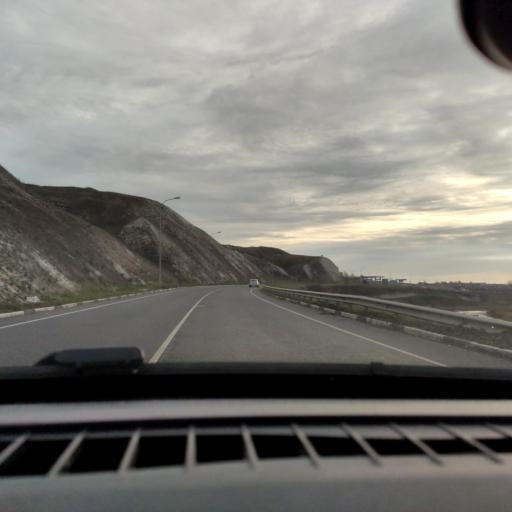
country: RU
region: Belgorod
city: Alekseyevka
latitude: 50.6411
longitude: 38.6627
